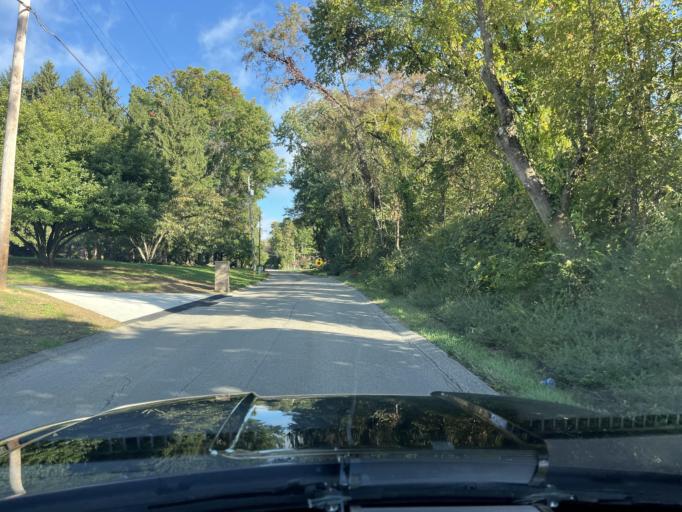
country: US
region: Pennsylvania
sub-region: Fayette County
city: South Uniontown
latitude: 39.8856
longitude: -79.7550
